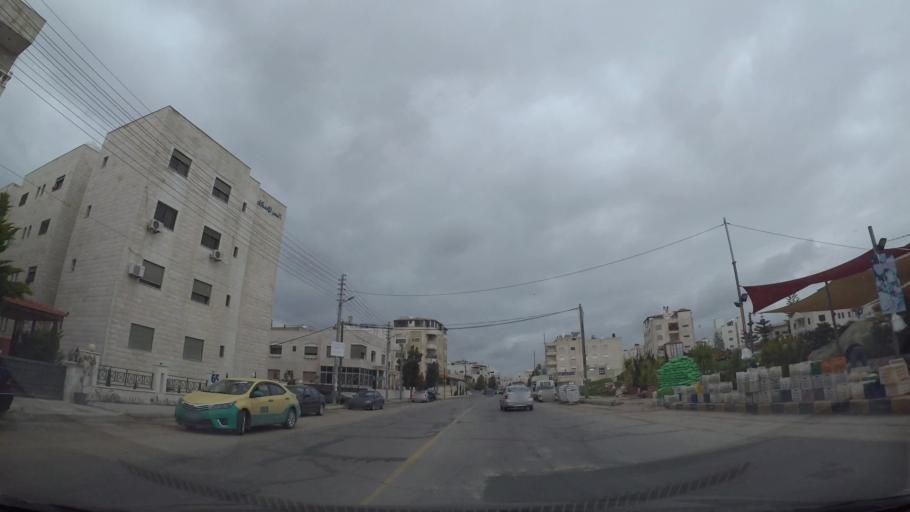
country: JO
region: Amman
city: Wadi as Sir
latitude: 31.9625
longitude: 35.8347
